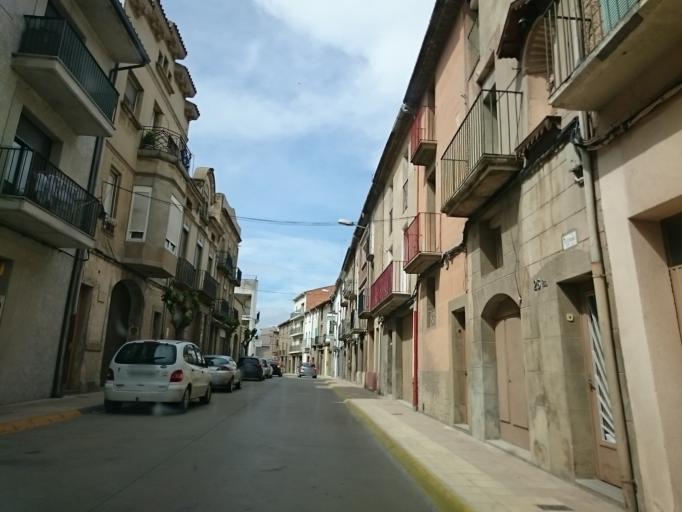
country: ES
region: Catalonia
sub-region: Provincia de Lleida
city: Ivorra
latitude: 41.7857
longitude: 1.2899
